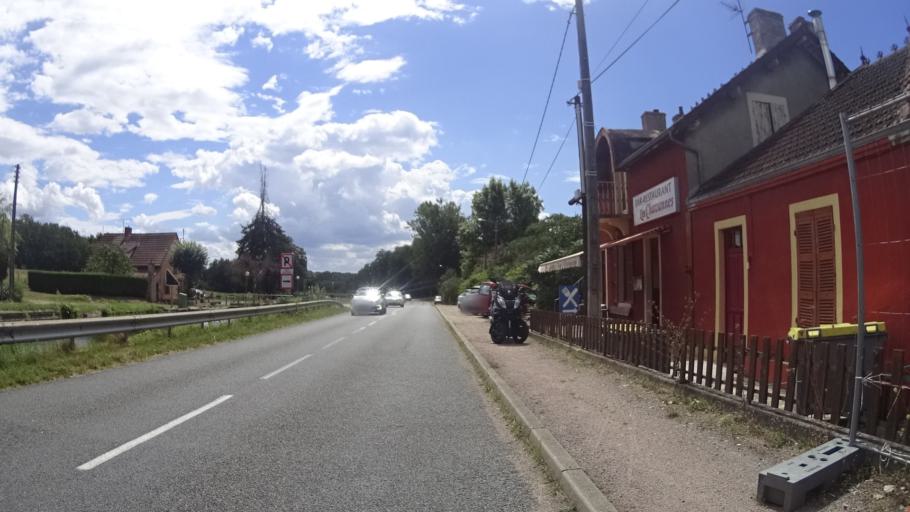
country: FR
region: Bourgogne
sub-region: Departement de Saone-et-Loire
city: Montceau-les-Mines
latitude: 46.6543
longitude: 4.3401
